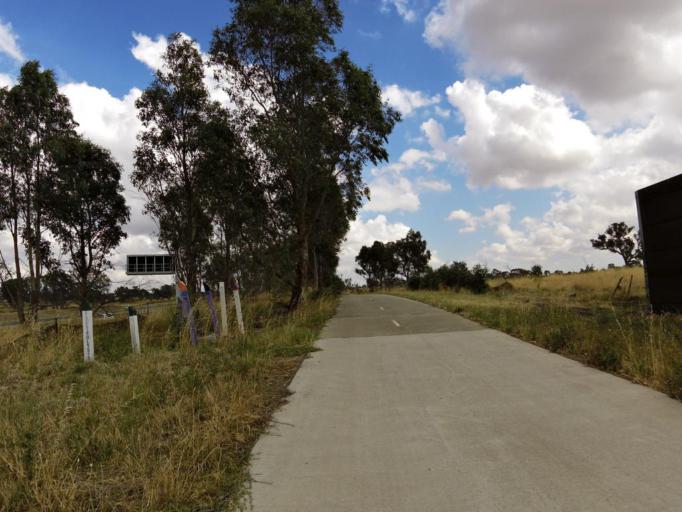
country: AU
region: Victoria
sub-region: Hume
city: Craigieburn
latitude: -37.6191
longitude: 144.9913
